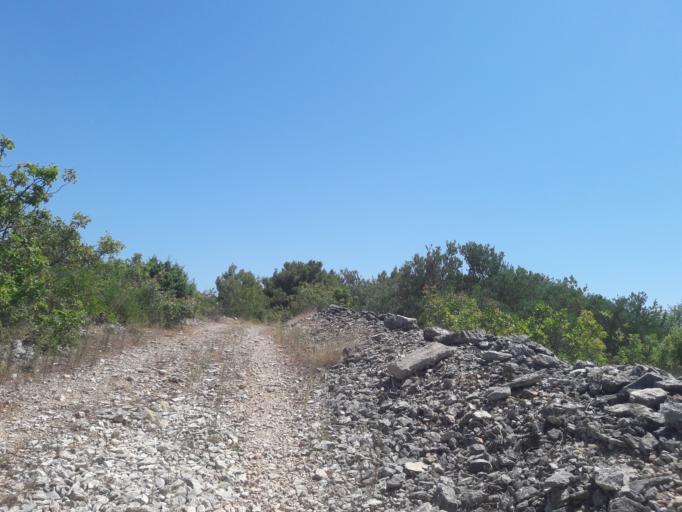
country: HR
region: Sibensko-Kniniska
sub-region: Grad Sibenik
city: Sibenik
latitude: 43.6928
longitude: 15.8542
